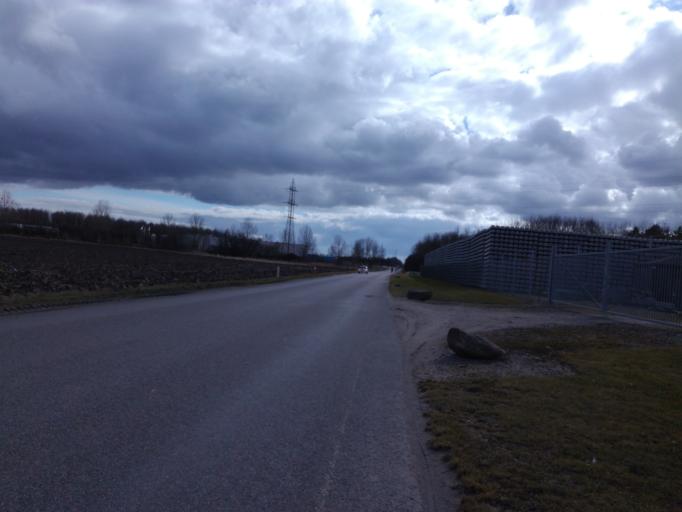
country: DK
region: South Denmark
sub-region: Fredericia Kommune
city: Fredericia
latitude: 55.5888
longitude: 9.7350
